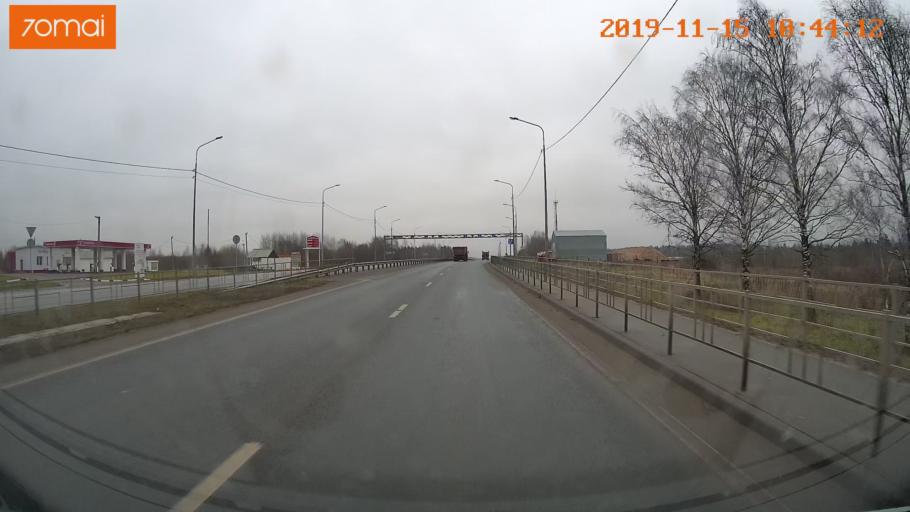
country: RU
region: Vologda
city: Sheksna
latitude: 59.2115
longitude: 38.5523
